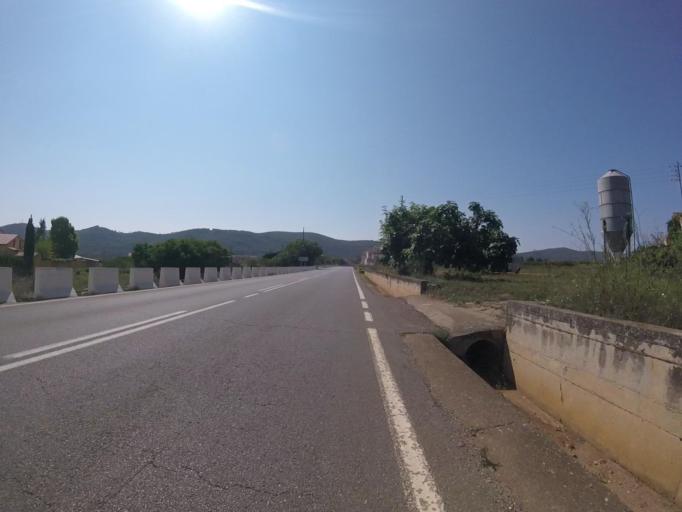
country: ES
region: Valencia
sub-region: Provincia de Castello
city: Adzaneta
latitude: 40.2223
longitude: -0.1723
